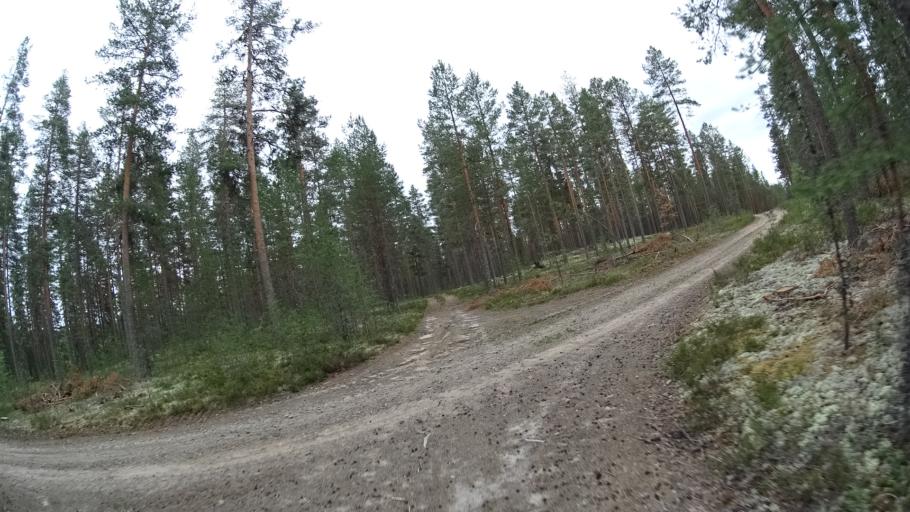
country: FI
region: Satakunta
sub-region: Pohjois-Satakunta
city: Jaemijaervi
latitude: 61.7636
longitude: 22.7530
